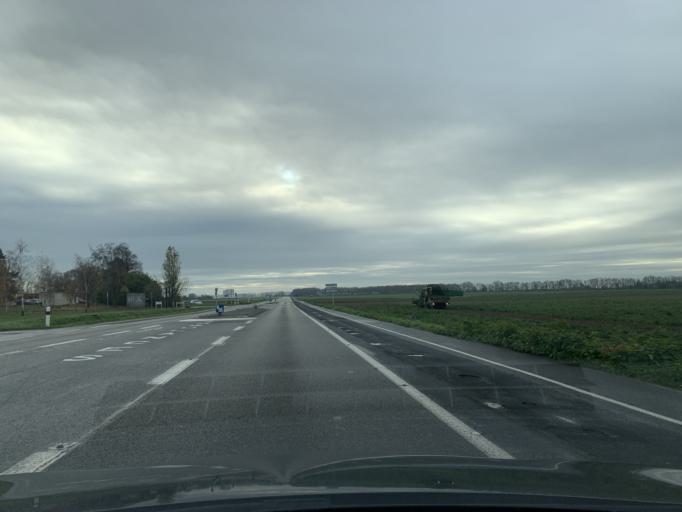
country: FR
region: Nord-Pas-de-Calais
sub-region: Departement du Nord
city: Goeulzin
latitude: 50.3370
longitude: 3.0997
